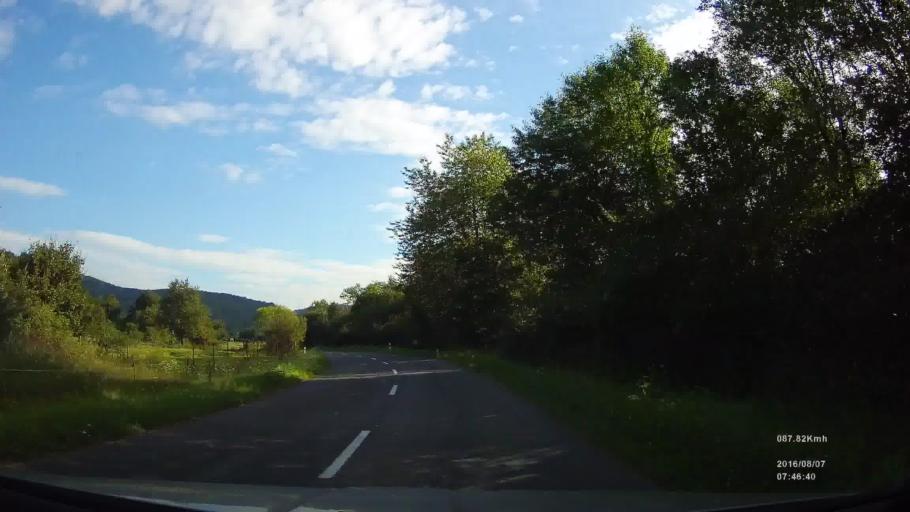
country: SK
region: Presovsky
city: Stropkov
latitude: 49.2724
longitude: 21.7515
